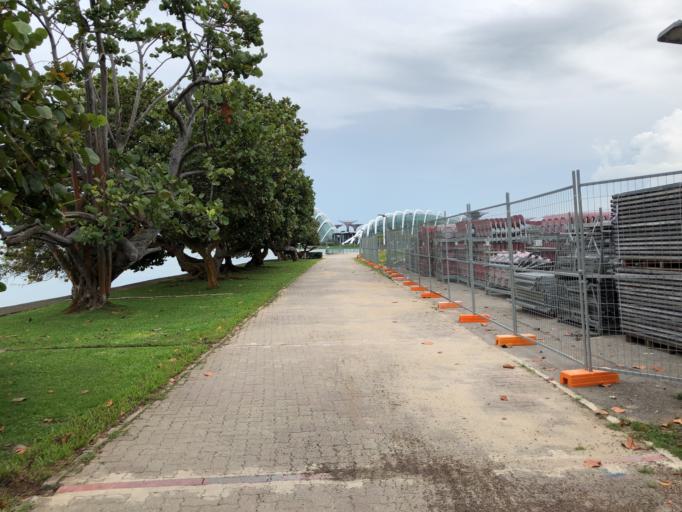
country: SG
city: Singapore
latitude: 1.2905
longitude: 103.8648
